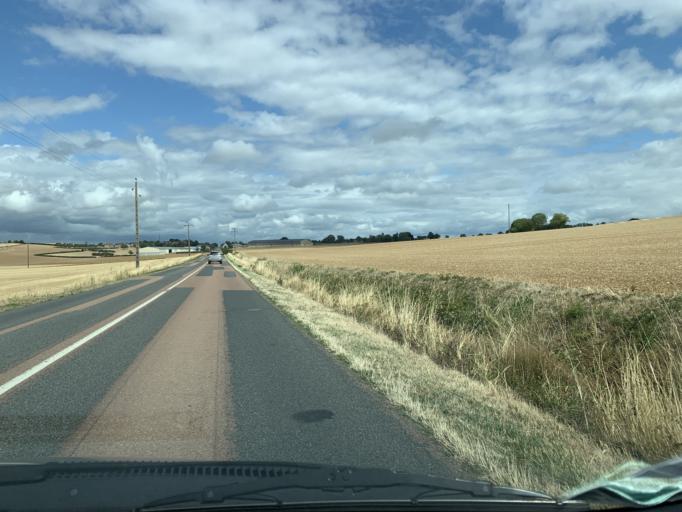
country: FR
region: Bourgogne
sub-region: Departement de la Nievre
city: Varzy
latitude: 47.3689
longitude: 3.4171
